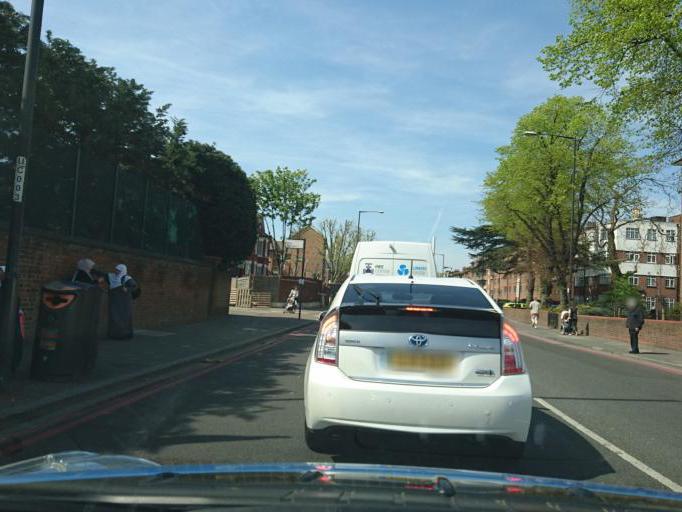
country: GB
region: England
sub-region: Greater London
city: Hackney
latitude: 51.5674
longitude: -0.0609
